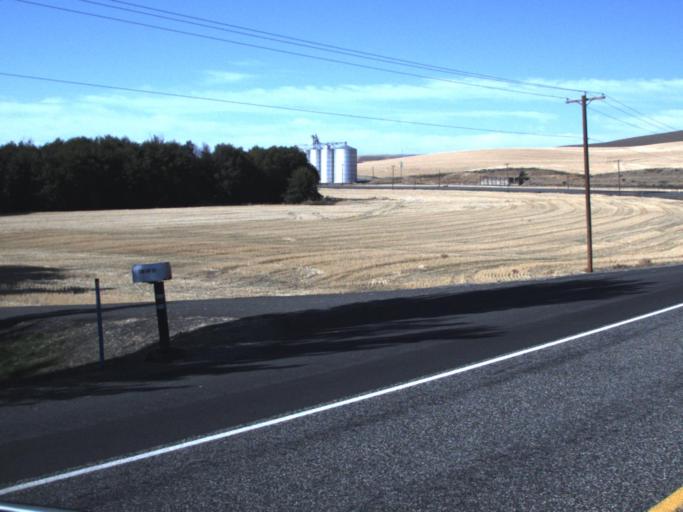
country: US
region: Washington
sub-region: Walla Walla County
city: Waitsburg
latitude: 46.2752
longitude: -118.2211
